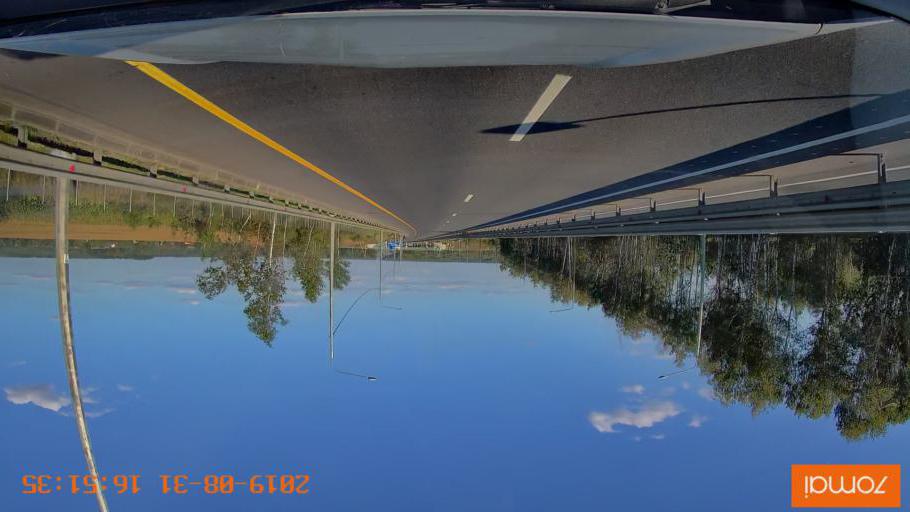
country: RU
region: Kaluga
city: Pyatovskiy
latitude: 54.7289
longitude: 36.1740
